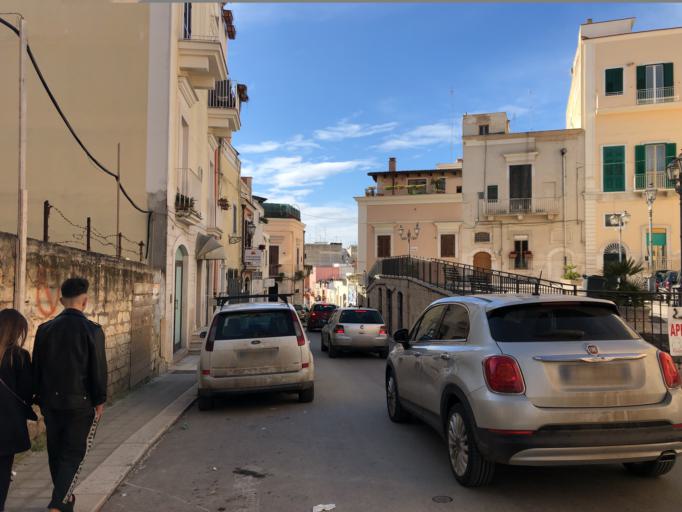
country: IT
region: Apulia
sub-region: Provincia di Barletta - Andria - Trani
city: Andria
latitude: 41.2277
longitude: 16.2944
